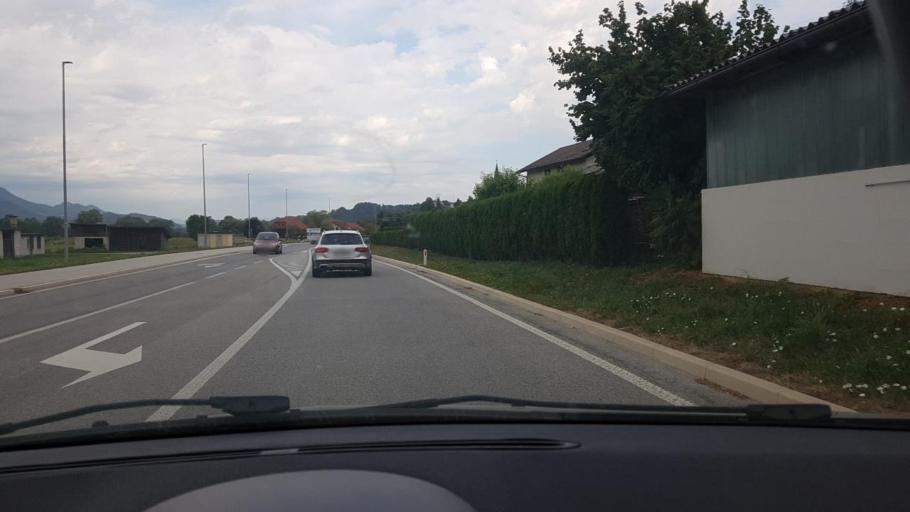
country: SI
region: Sentjur pri Celju
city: Sentjur
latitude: 46.2123
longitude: 15.4306
